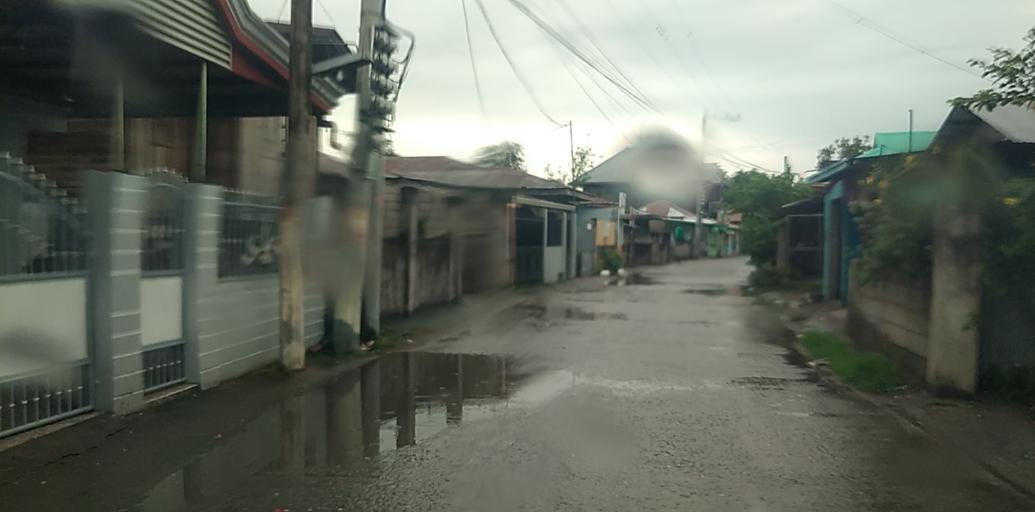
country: PH
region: Central Luzon
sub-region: Province of Pampanga
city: Arayat
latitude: 15.1361
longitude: 120.7406
